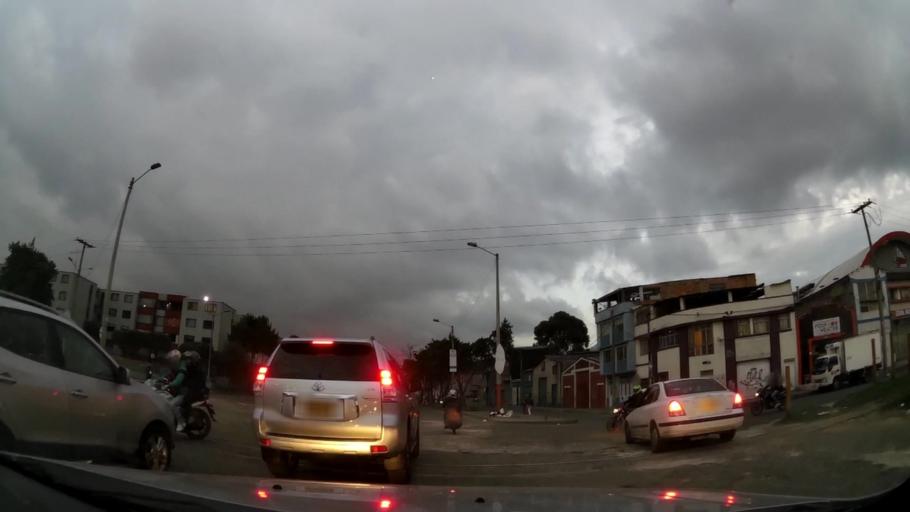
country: CO
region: Bogota D.C.
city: Bogota
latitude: 4.6181
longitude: -74.0841
